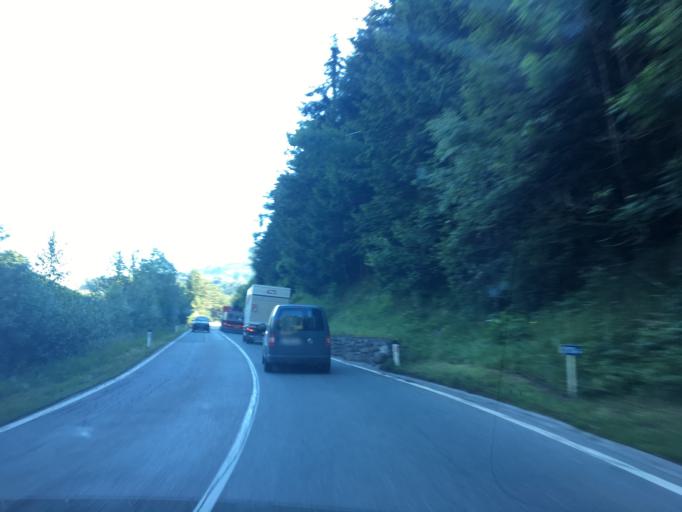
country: AT
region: Tyrol
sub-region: Politischer Bezirk Innsbruck Land
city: Patsch
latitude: 47.1933
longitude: 11.4021
